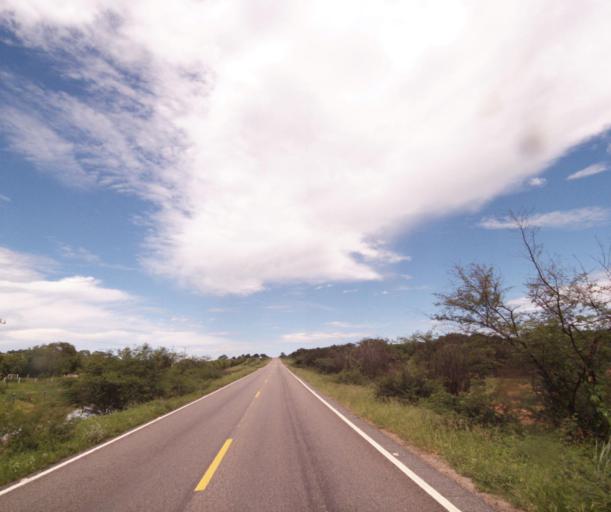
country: BR
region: Bahia
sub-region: Guanambi
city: Guanambi
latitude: -14.2335
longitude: -42.9625
